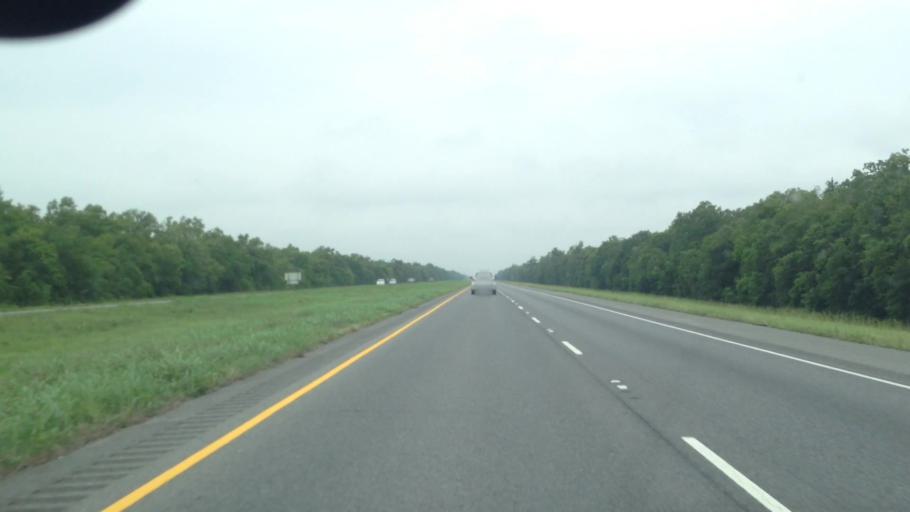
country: US
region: Louisiana
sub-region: Evangeline Parish
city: Ville Platte
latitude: 30.7354
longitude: -92.1342
